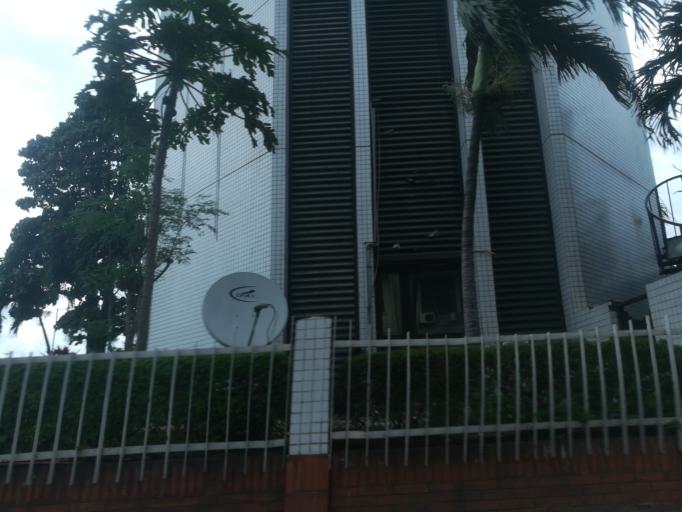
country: NG
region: Lagos
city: Lagos
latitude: 6.4485
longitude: 3.3942
